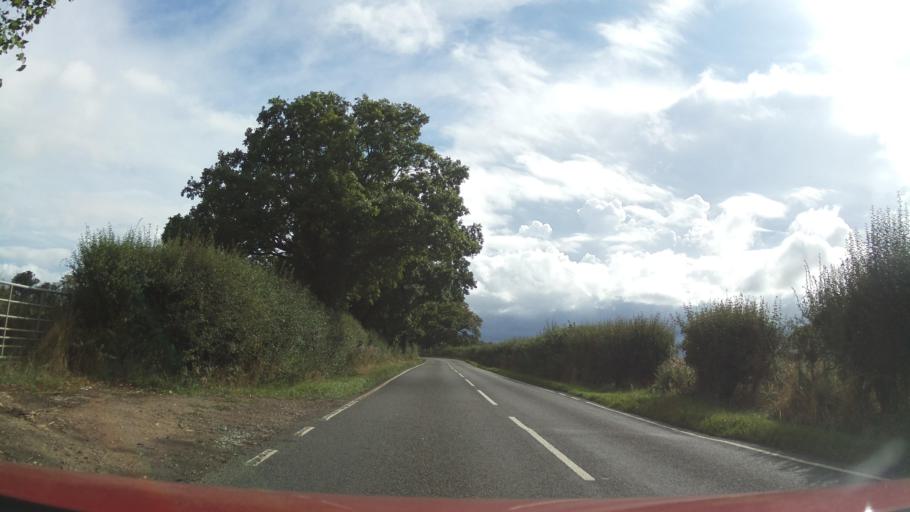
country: GB
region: England
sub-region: Telford and Wrekin
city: Madeley
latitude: 52.6354
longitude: -2.4137
